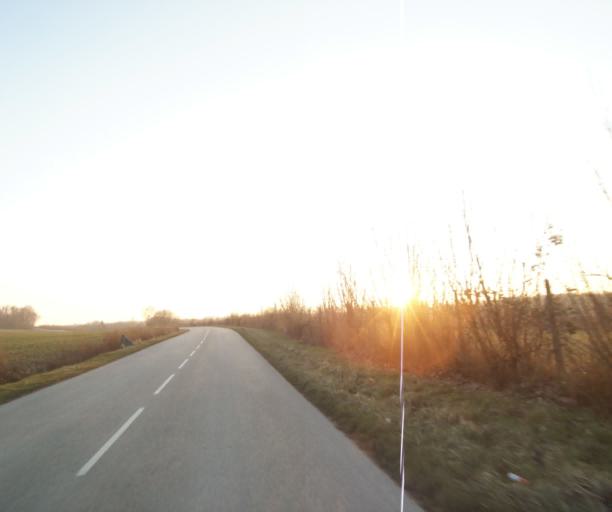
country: FR
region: Champagne-Ardenne
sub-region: Departement de la Haute-Marne
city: Bienville
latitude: 48.5960
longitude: 5.0424
